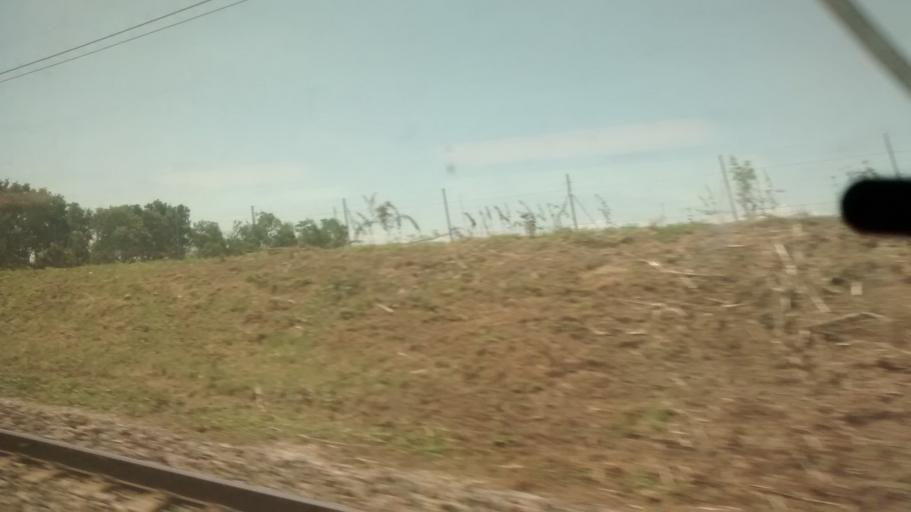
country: FR
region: Rhone-Alpes
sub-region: Departement de l'Ain
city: Civrieux
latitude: 45.9340
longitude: 4.8685
